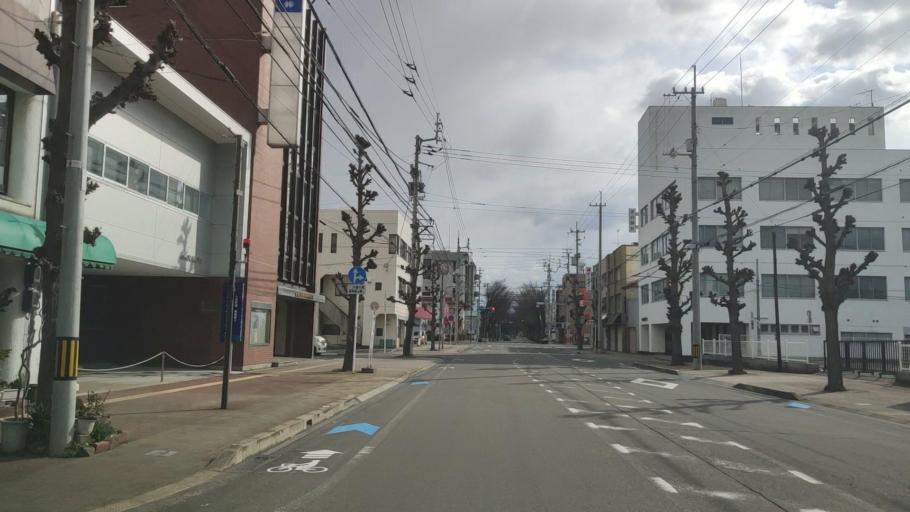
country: JP
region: Ehime
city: Hojo
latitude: 34.0637
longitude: 132.9958
